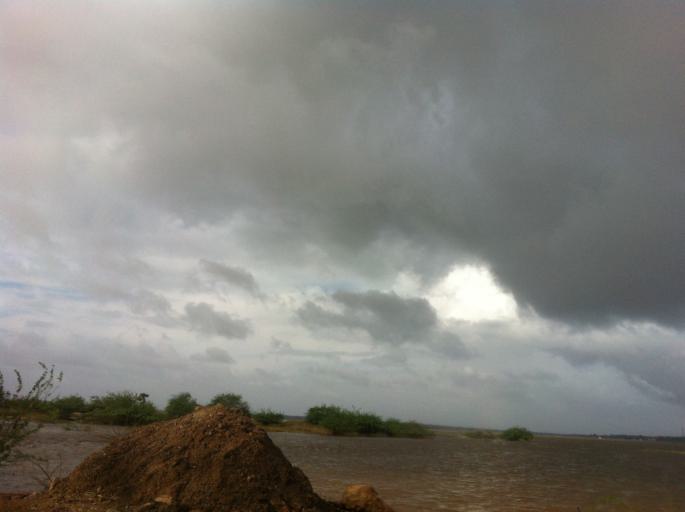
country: IN
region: Tamil Nadu
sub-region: Villupuram
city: Marakkanam
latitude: 12.1999
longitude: 79.9598
